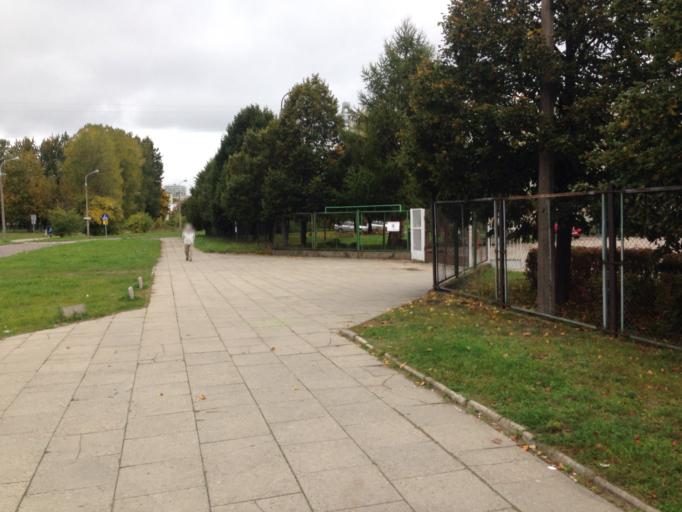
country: PL
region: Pomeranian Voivodeship
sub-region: Sopot
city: Sopot
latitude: 54.4014
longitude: 18.6037
